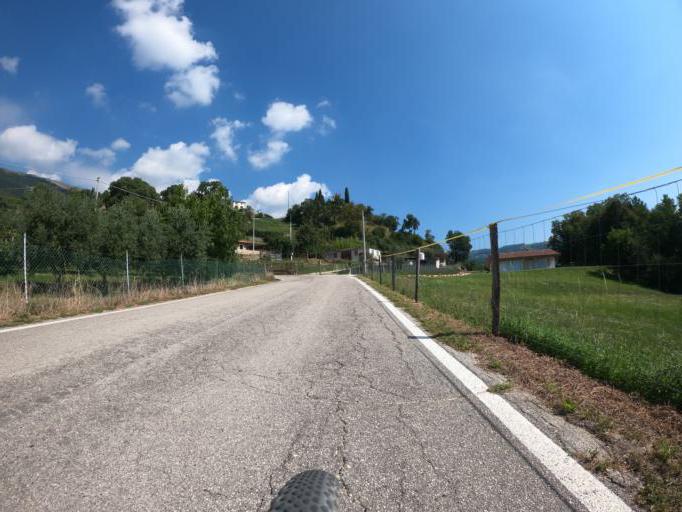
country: IT
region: Veneto
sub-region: Provincia di Verona
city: Caprino Veronese
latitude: 45.6270
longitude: 10.8252
